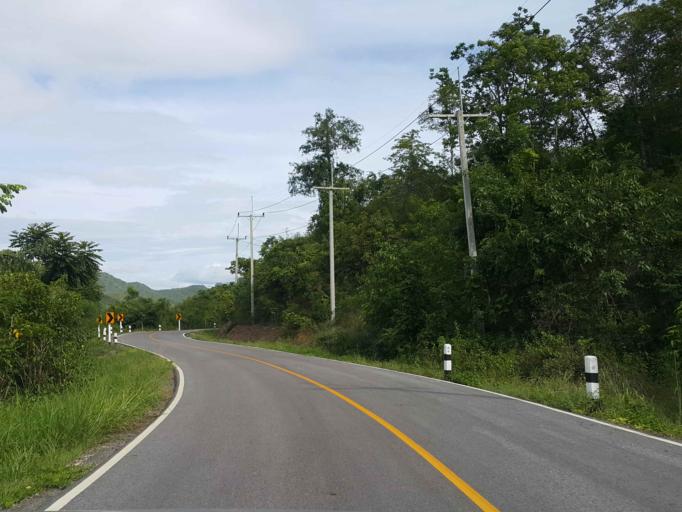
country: TH
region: Sukhothai
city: Thung Saliam
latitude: 17.2412
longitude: 99.4950
